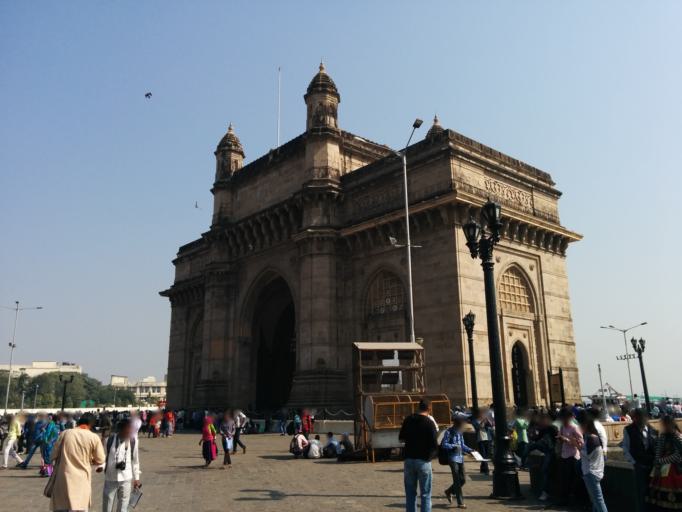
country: IN
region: Maharashtra
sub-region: Raigarh
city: Uran
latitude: 18.9220
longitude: 72.8340
